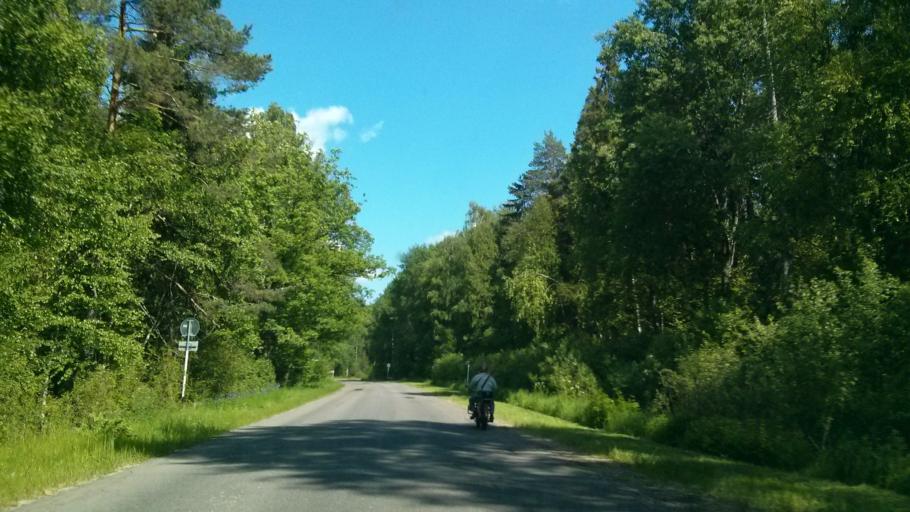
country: RU
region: Vladimir
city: Melenki
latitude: 55.3318
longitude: 41.6917
